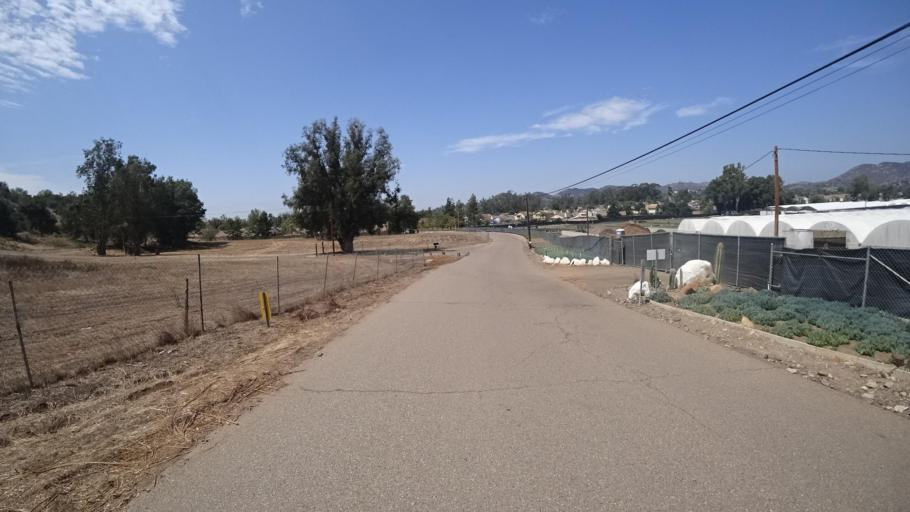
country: US
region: California
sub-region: San Diego County
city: Escondido
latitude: 33.1673
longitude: -117.0785
